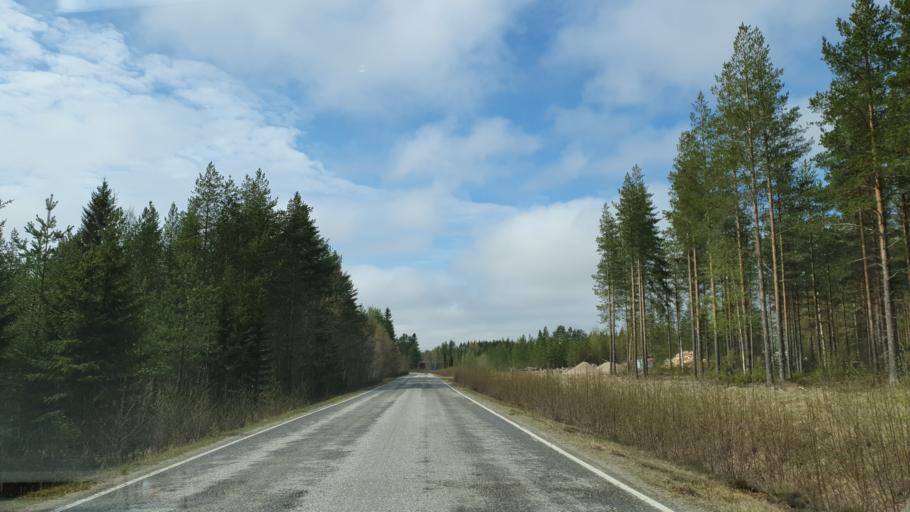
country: FI
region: Kainuu
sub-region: Kehys-Kainuu
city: Kuhmo
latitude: 64.1277
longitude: 29.5993
